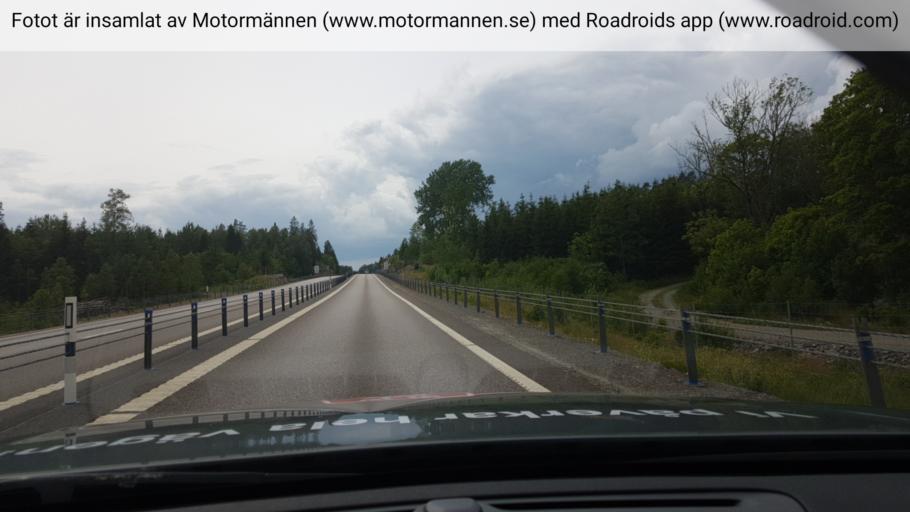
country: SE
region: OErebro
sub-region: Askersunds Kommun
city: Askersund
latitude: 58.8176
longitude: 14.8691
